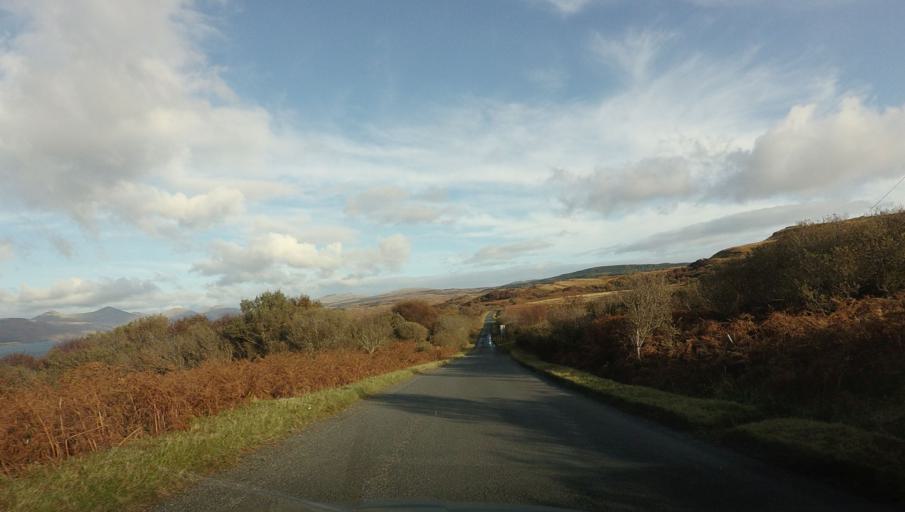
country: GB
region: Scotland
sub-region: Argyll and Bute
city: Isle Of Mull
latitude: 56.3437
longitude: -6.1205
